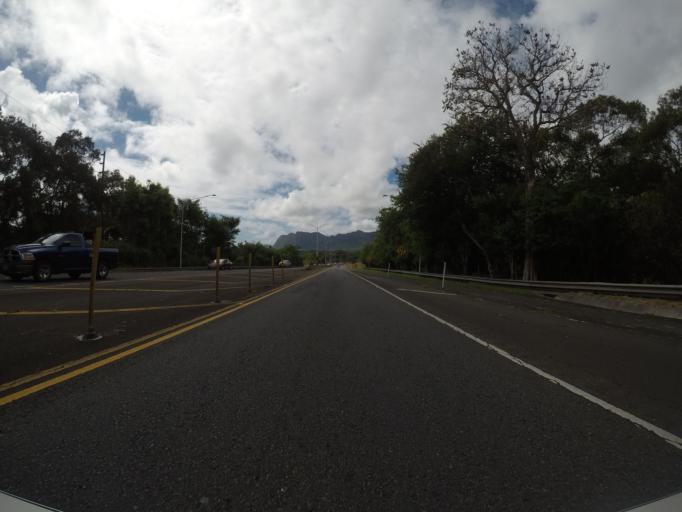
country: US
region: Hawaii
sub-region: Honolulu County
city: Waimanalo
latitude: 21.3571
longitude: -157.7321
